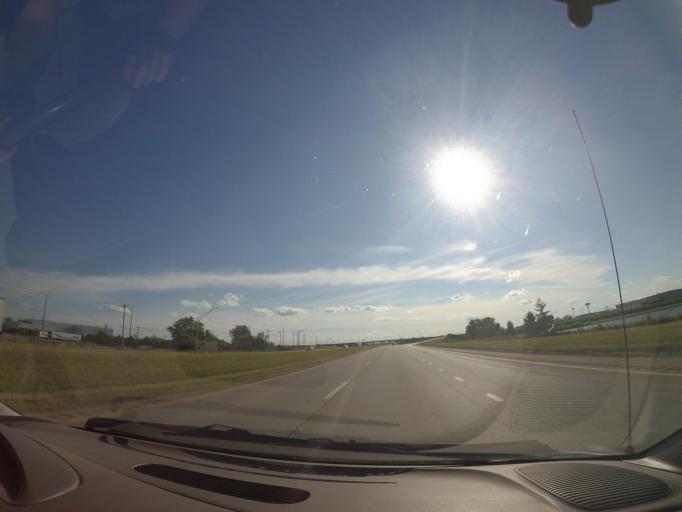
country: US
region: Ohio
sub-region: Henry County
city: Napoleon
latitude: 41.4156
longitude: -84.1002
